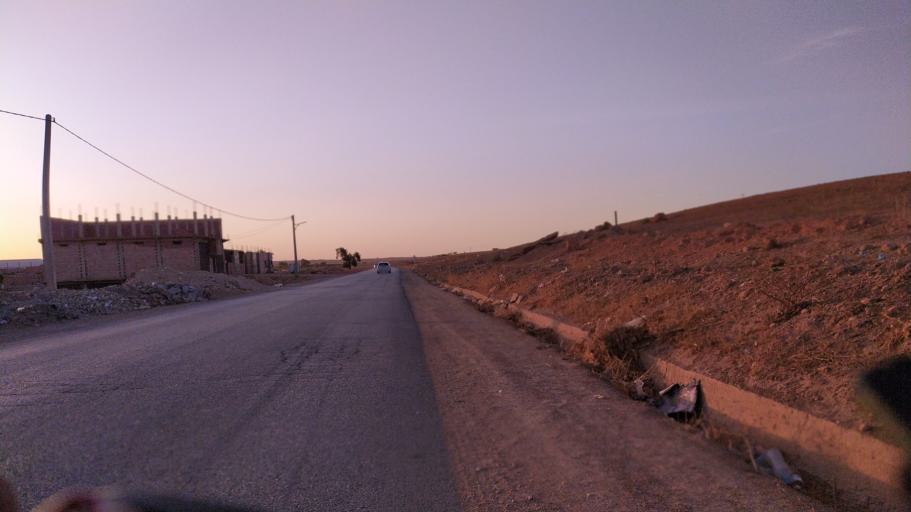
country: DZ
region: Tiaret
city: Frenda
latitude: 34.9002
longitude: 1.2442
